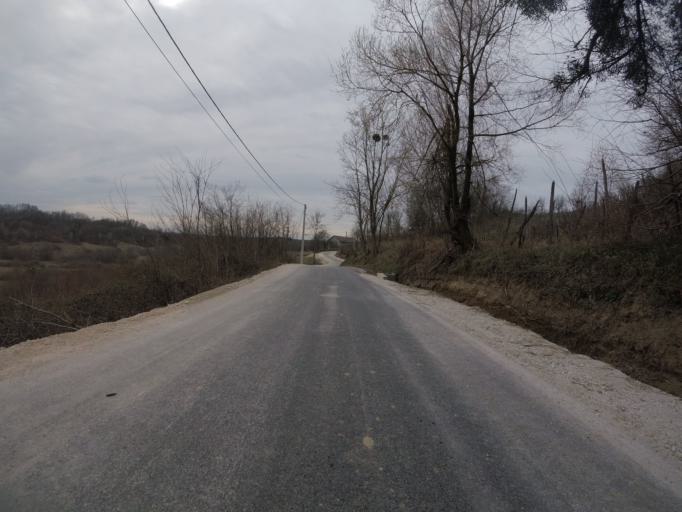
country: HR
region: Grad Zagreb
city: Strmec
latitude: 45.6111
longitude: 15.9123
